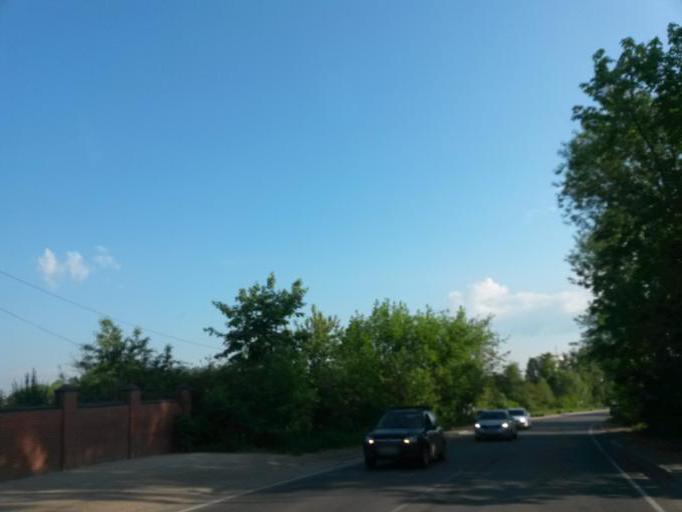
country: RU
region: Moskovskaya
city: Yam
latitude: 55.4652
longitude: 37.7017
